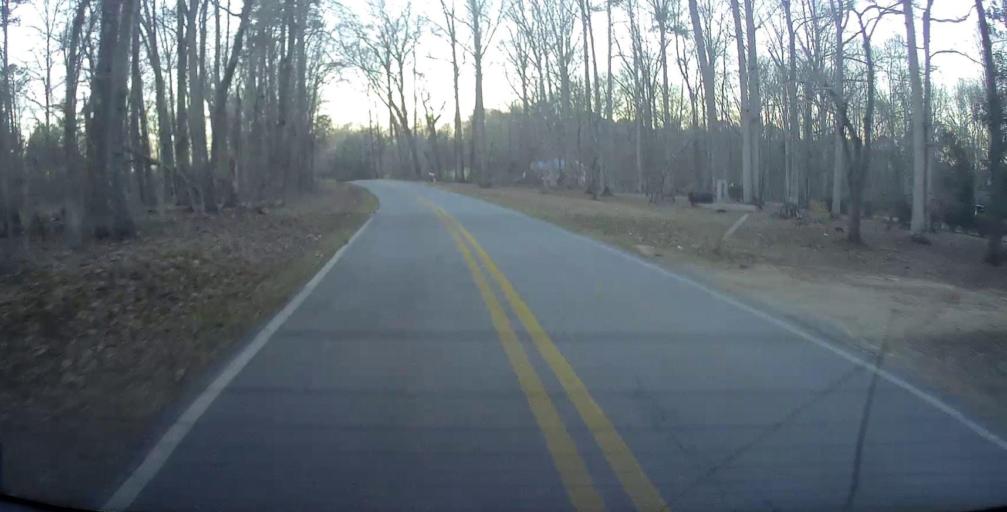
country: US
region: Georgia
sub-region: Troup County
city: La Grange
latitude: 33.0533
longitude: -84.9699
